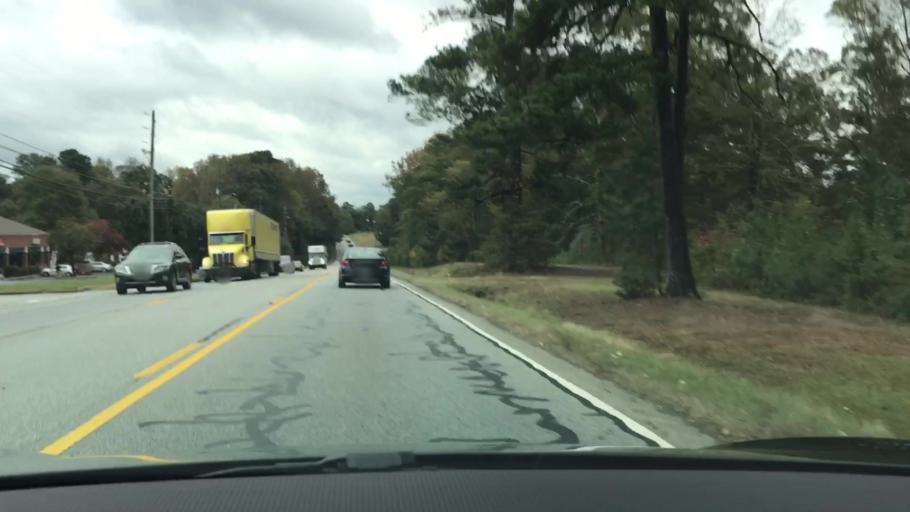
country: US
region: Georgia
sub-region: Oconee County
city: Watkinsville
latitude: 33.8722
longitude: -83.4369
